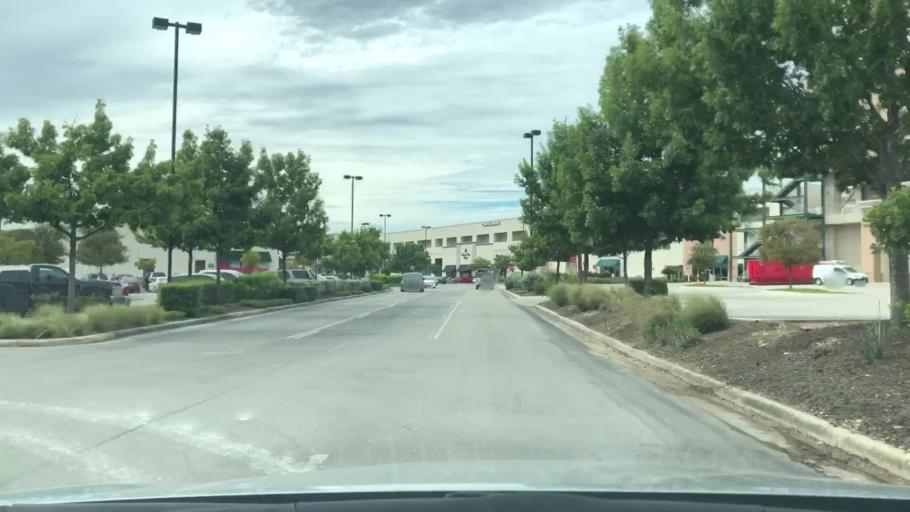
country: US
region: Texas
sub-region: Bexar County
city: Castle Hills
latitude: 29.5172
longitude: -98.5026
